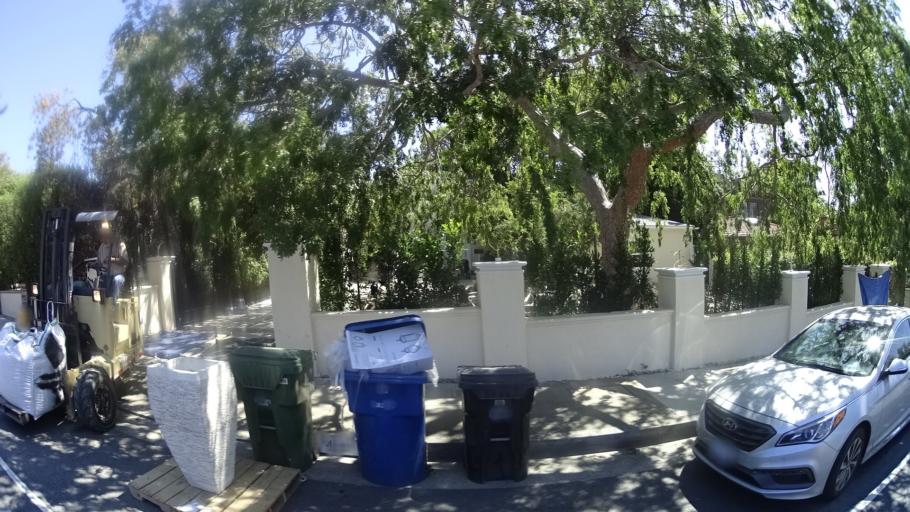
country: US
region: California
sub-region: Los Angeles County
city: Santa Monica
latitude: 34.0452
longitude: -118.4882
